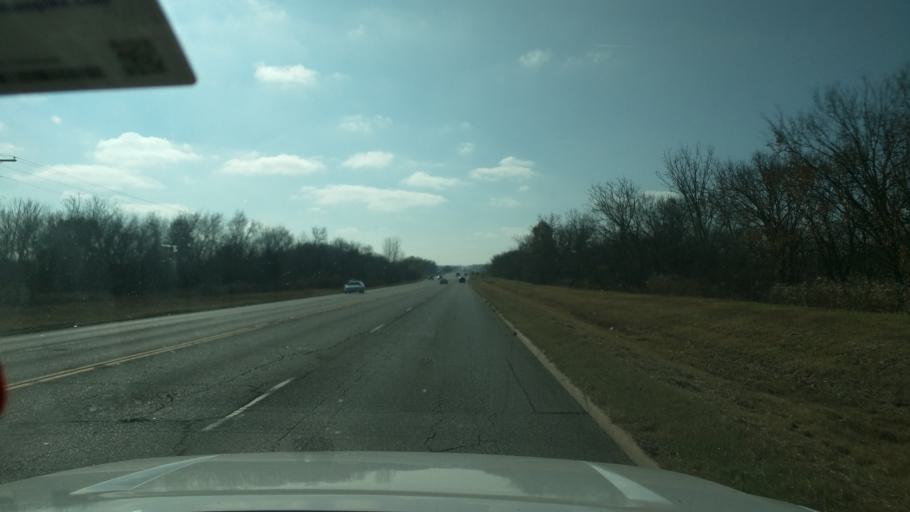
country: US
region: Oklahoma
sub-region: Washington County
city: Bartlesville
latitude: 36.6748
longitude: -95.9353
